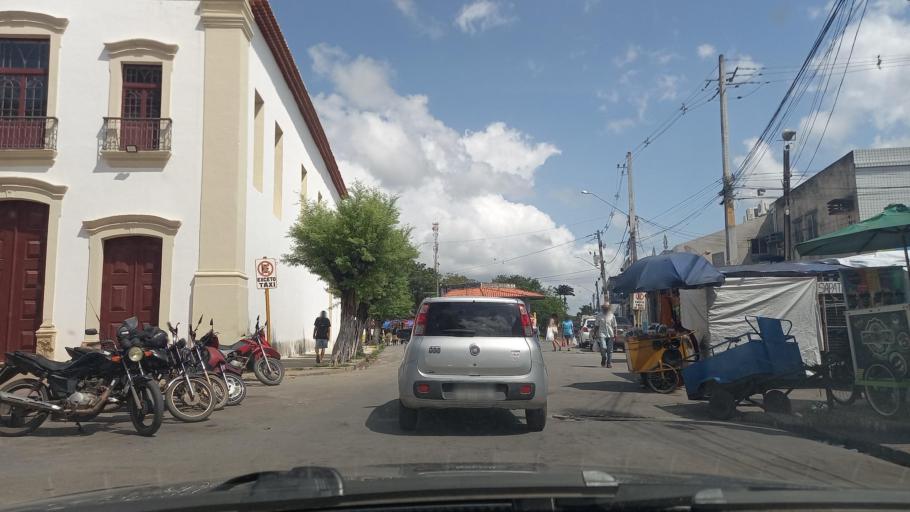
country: BR
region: Pernambuco
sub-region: Goiana
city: Goiana
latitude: -7.5607
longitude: -34.9992
